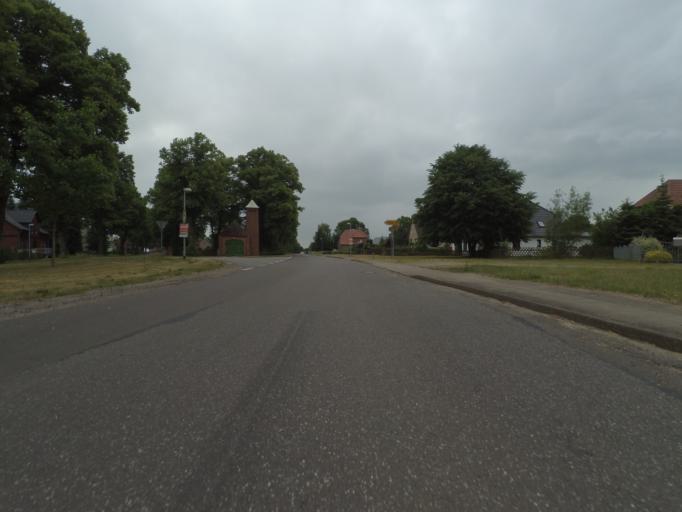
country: DE
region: Mecklenburg-Vorpommern
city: Spornitz
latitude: 53.3618
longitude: 11.6652
